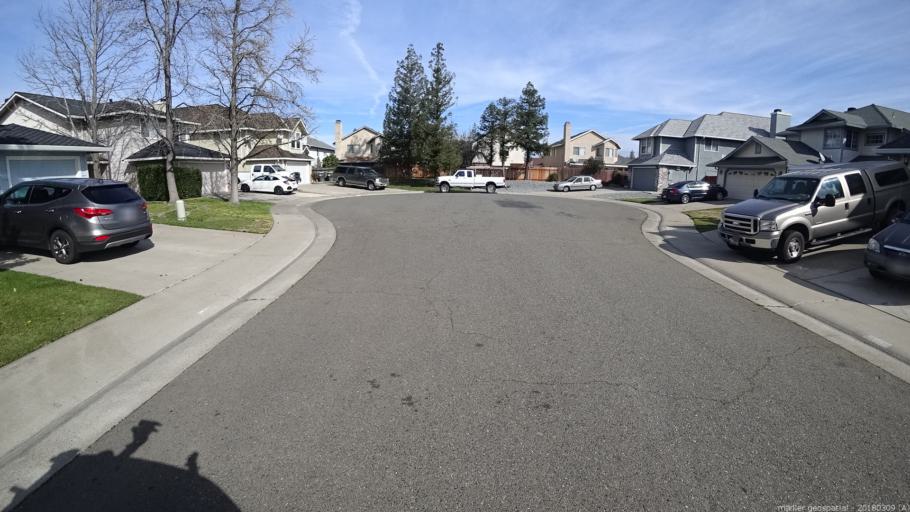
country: US
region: California
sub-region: Sacramento County
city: Florin
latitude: 38.4566
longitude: -121.3982
